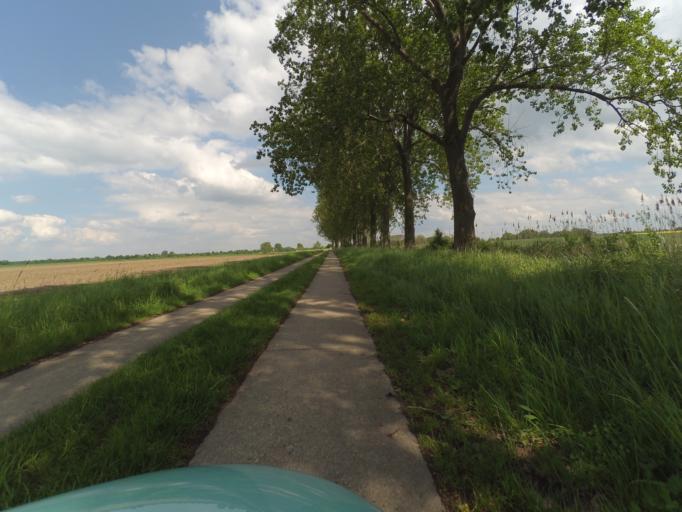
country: DE
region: Lower Saxony
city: Sehnde
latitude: 52.3067
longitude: 9.9177
